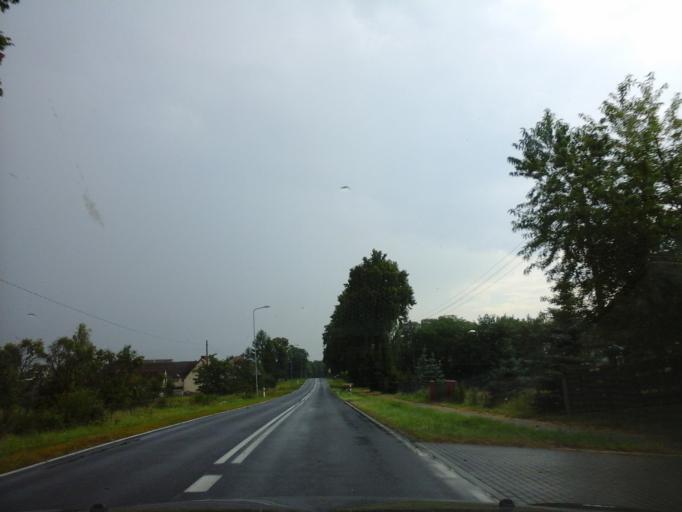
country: PL
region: Greater Poland Voivodeship
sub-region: Powiat miedzychodzki
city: Miedzychod
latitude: 52.5769
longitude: 15.8985
